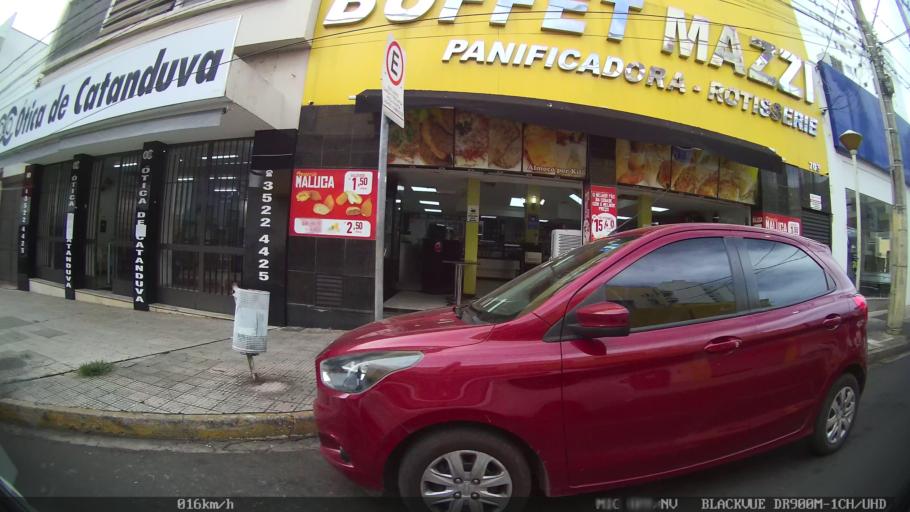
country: BR
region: Sao Paulo
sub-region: Catanduva
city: Catanduva
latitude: -21.1366
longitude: -48.9726
